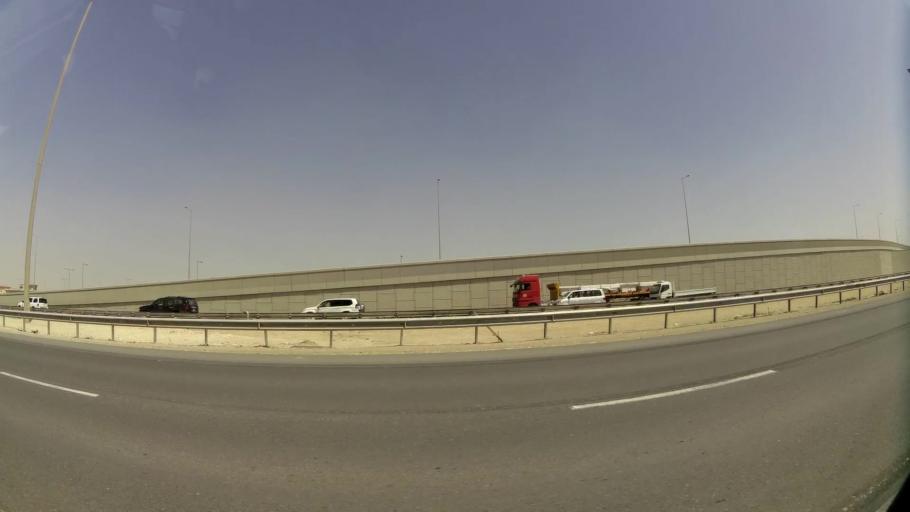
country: QA
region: Baladiyat Umm Salal
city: Umm Salal Muhammad
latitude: 25.3733
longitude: 51.4434
